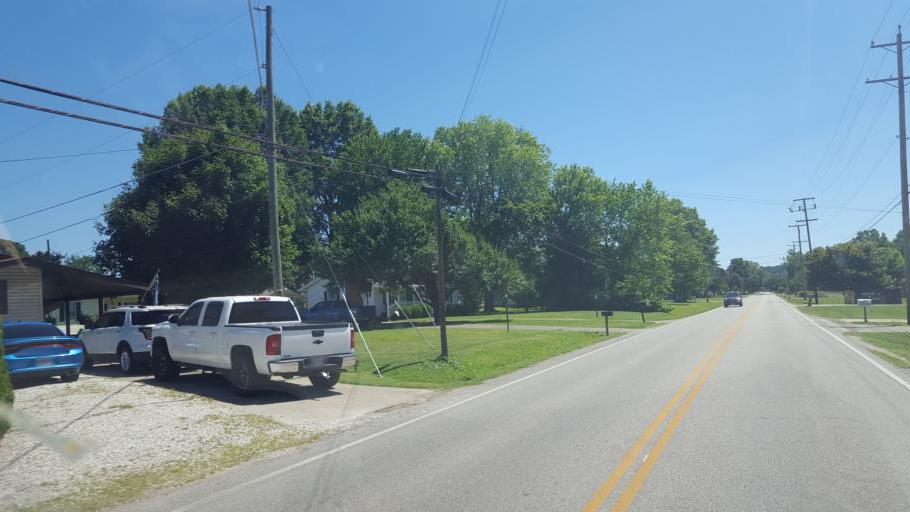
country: US
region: West Virginia
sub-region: Cabell County
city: Pea Ridge
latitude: 38.4419
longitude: -82.3475
